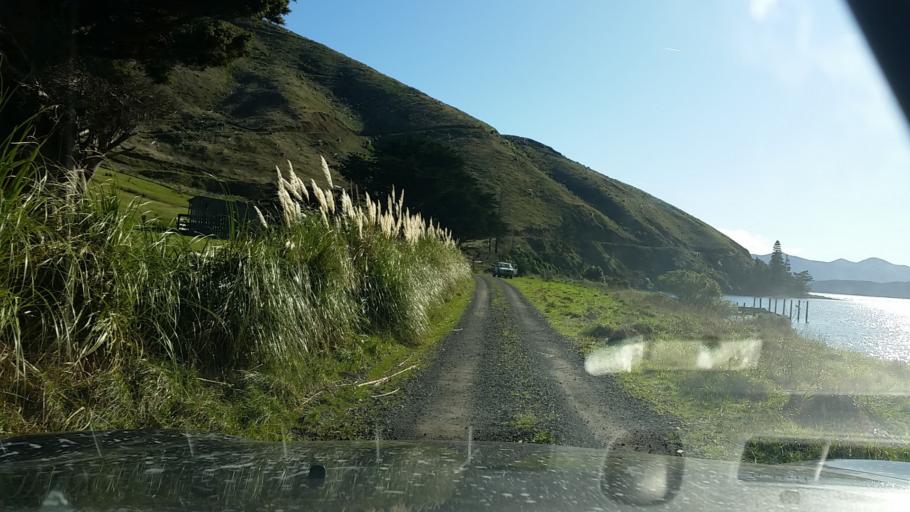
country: NZ
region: Marlborough
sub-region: Marlborough District
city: Picton
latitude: -41.1115
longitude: 174.0339
